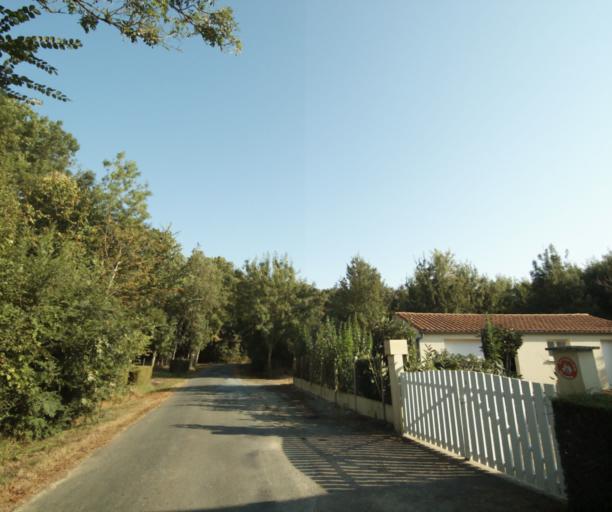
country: FR
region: Poitou-Charentes
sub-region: Departement de la Charente-Maritime
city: Cabariot
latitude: 45.9597
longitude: -0.8428
